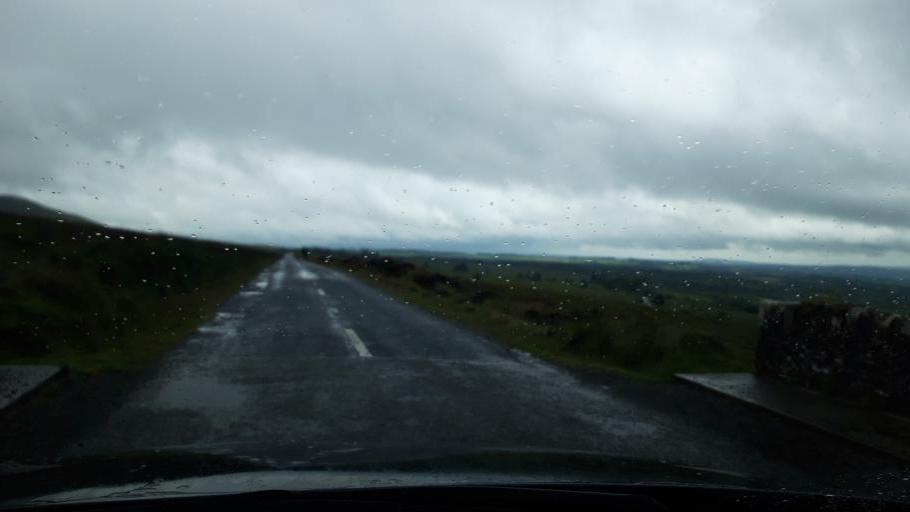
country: IE
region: Munster
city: Cahir
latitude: 52.2157
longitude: -7.9323
